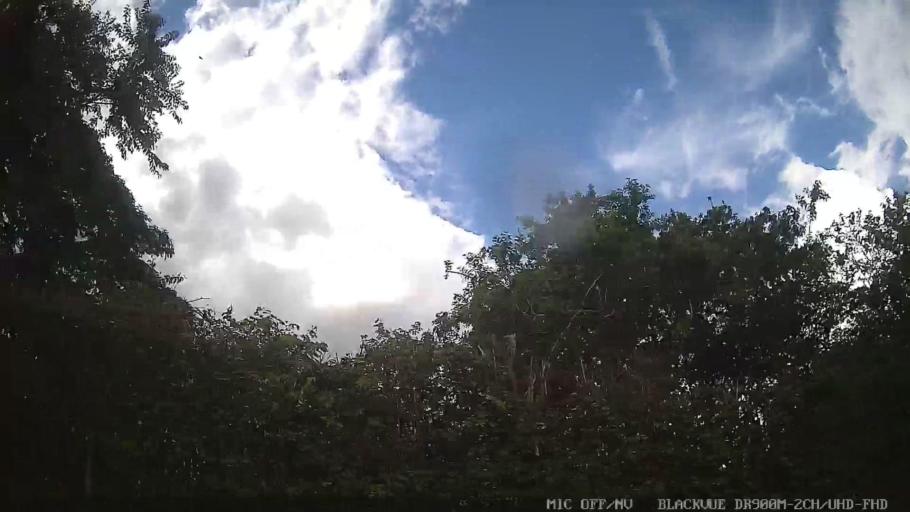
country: BR
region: Sao Paulo
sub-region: Jaguariuna
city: Jaguariuna
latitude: -22.6682
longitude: -47.0656
